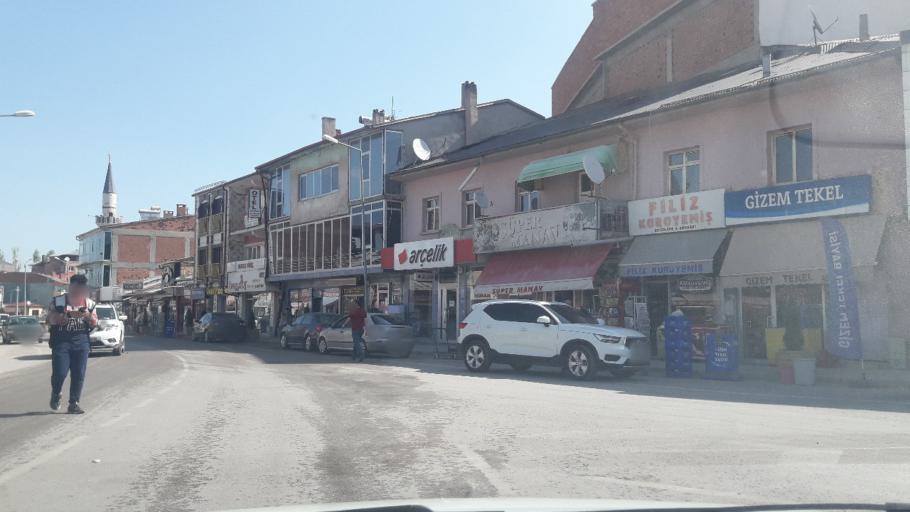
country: TR
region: Sivas
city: Kangal
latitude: 39.2344
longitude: 37.3911
